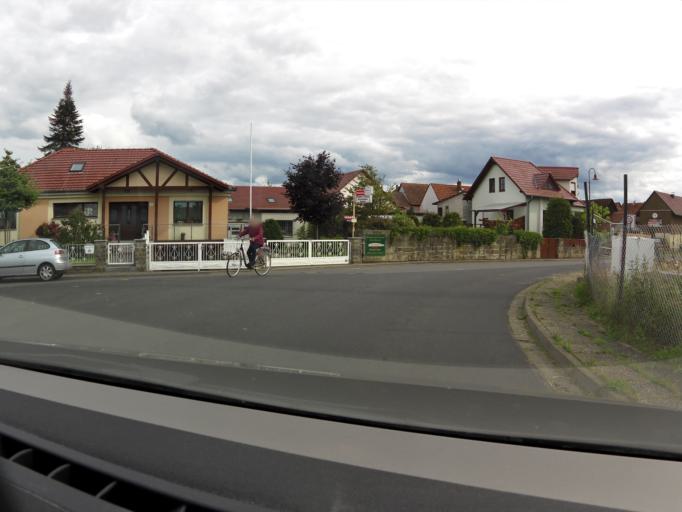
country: DE
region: Thuringia
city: Kammerforst
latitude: 51.1243
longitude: 10.4305
